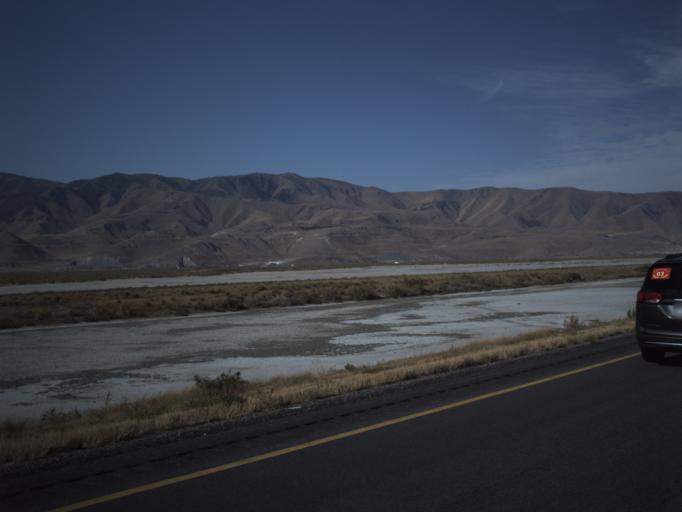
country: US
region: Utah
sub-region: Tooele County
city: Grantsville
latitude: 40.7037
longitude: -112.5031
